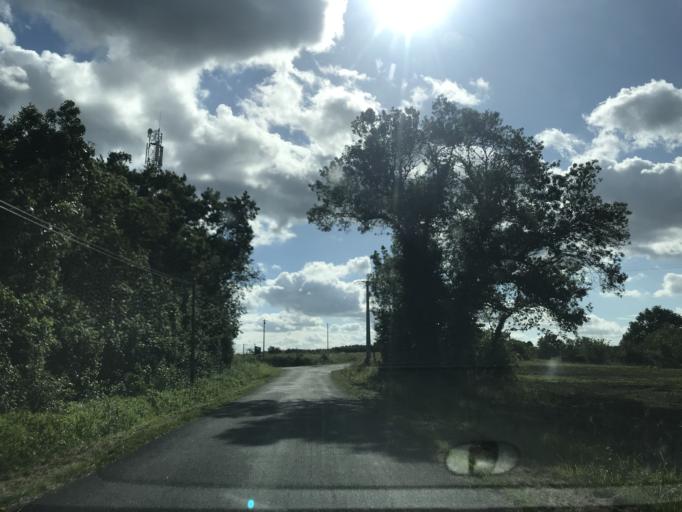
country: FR
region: Poitou-Charentes
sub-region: Departement de la Charente
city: Chalais
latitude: 45.2737
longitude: -0.0212
